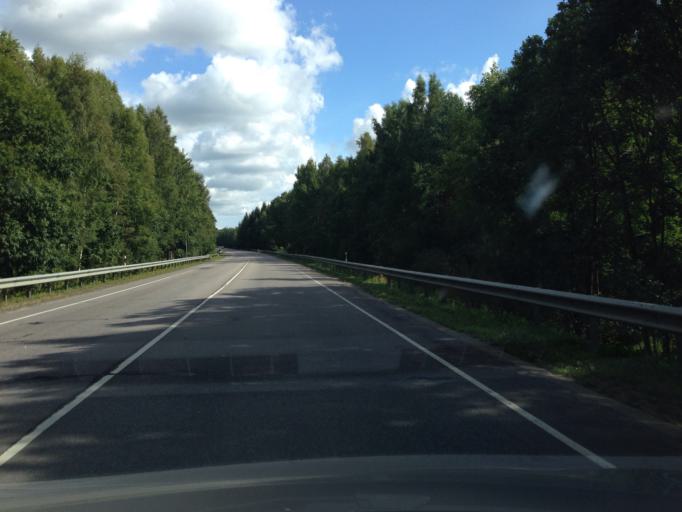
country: EE
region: Harju
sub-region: Saku vald
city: Saku
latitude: 59.3124
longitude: 24.6942
